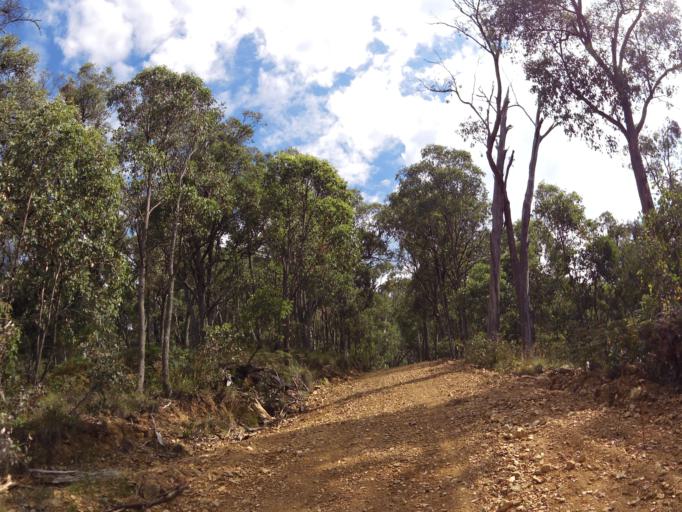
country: AU
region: Victoria
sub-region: Alpine
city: Mount Beauty
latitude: -36.7757
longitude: 147.0153
